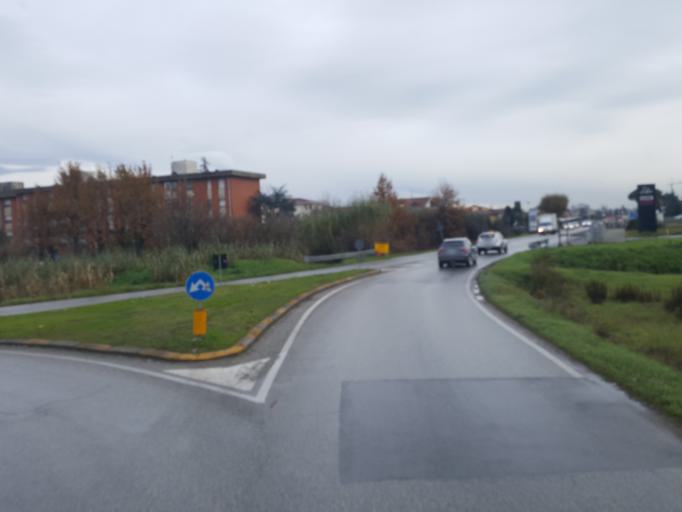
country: IT
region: Tuscany
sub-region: Provincia di Lucca
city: Porcari
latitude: 43.8342
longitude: 10.6160
